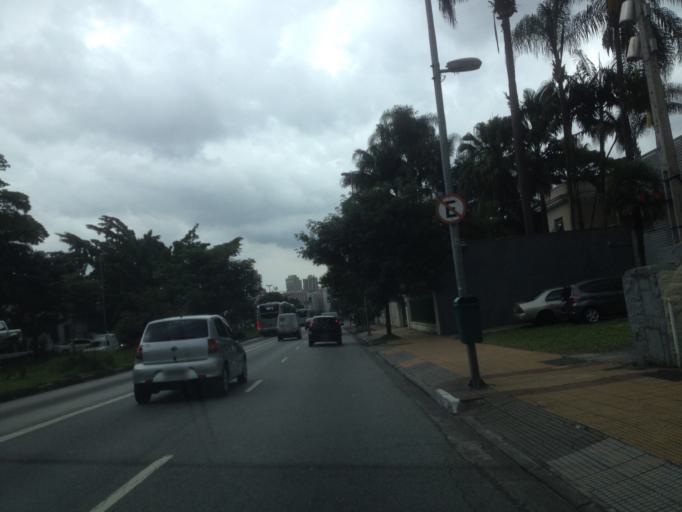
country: BR
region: Sao Paulo
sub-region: Sao Paulo
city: Sao Paulo
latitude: -23.5716
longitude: -46.6640
